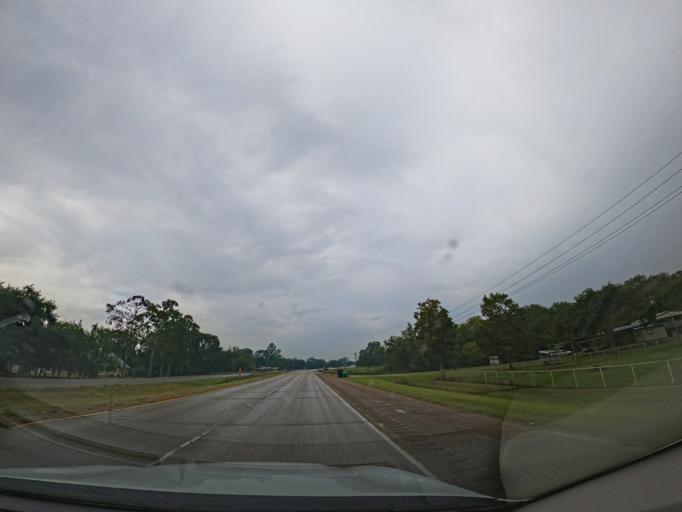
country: US
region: Louisiana
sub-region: Iberia Parish
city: Delcambre
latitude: 29.9690
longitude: -91.9069
